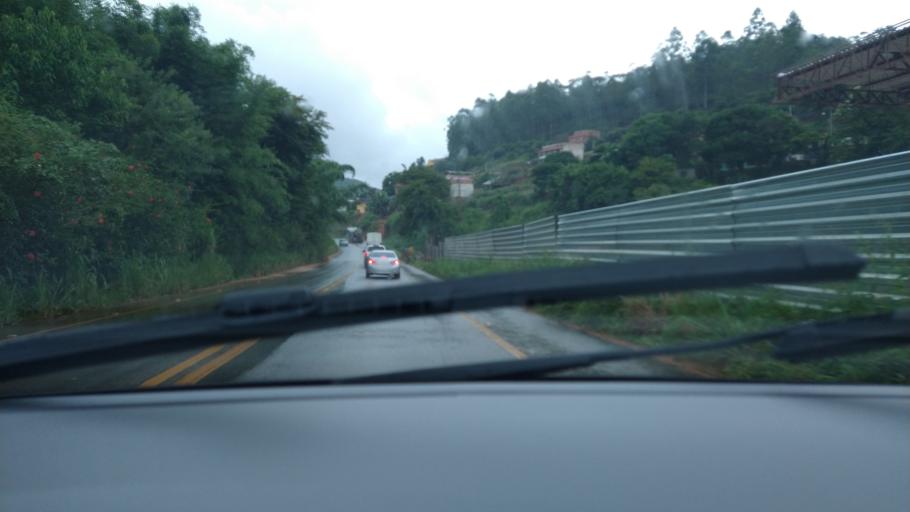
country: BR
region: Minas Gerais
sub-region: Vicosa
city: Vicosa
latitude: -20.6389
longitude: -42.8667
